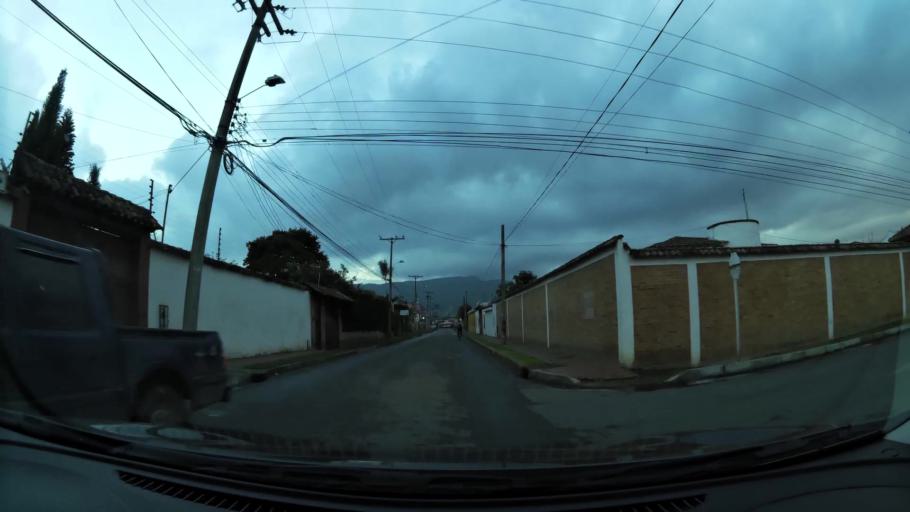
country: CO
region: Cundinamarca
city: Chia
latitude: 4.8480
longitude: -74.0608
